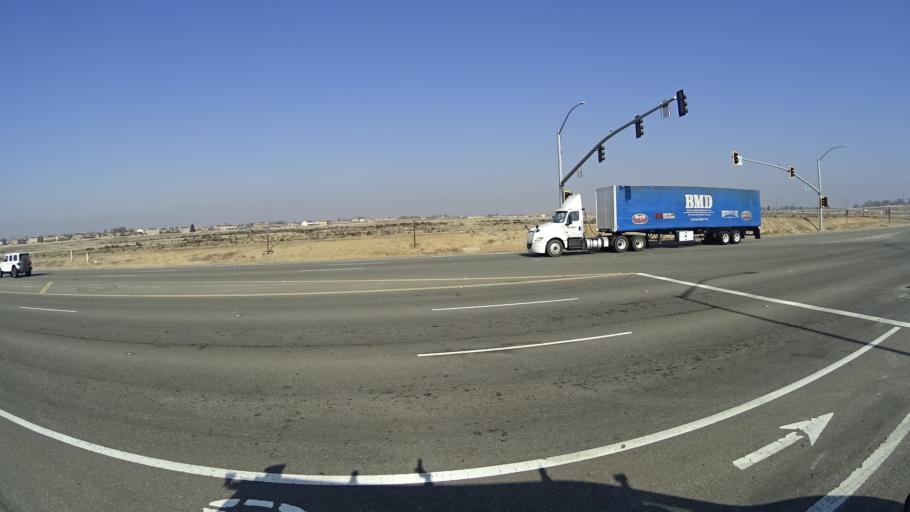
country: US
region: California
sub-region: Kern County
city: Bakersfield
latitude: 35.3980
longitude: -118.8829
